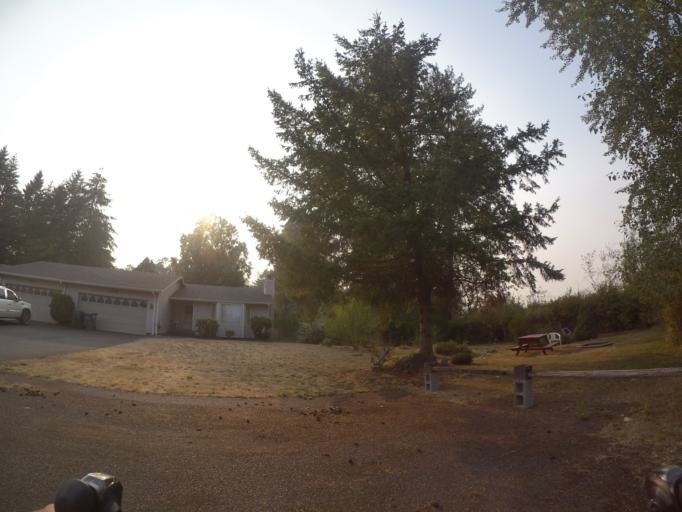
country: US
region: Washington
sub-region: Pierce County
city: Lakewood
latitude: 47.1818
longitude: -122.5143
